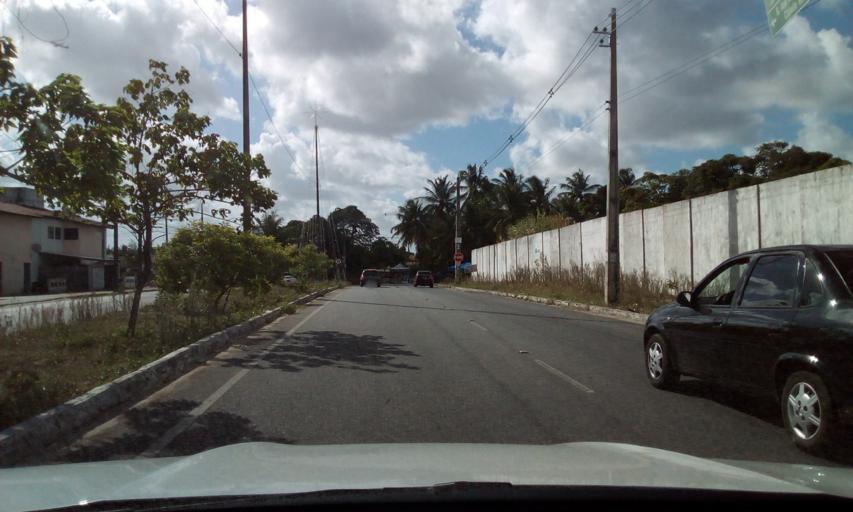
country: BR
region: Paraiba
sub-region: Bayeux
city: Bayeux
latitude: -7.1767
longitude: -34.9122
